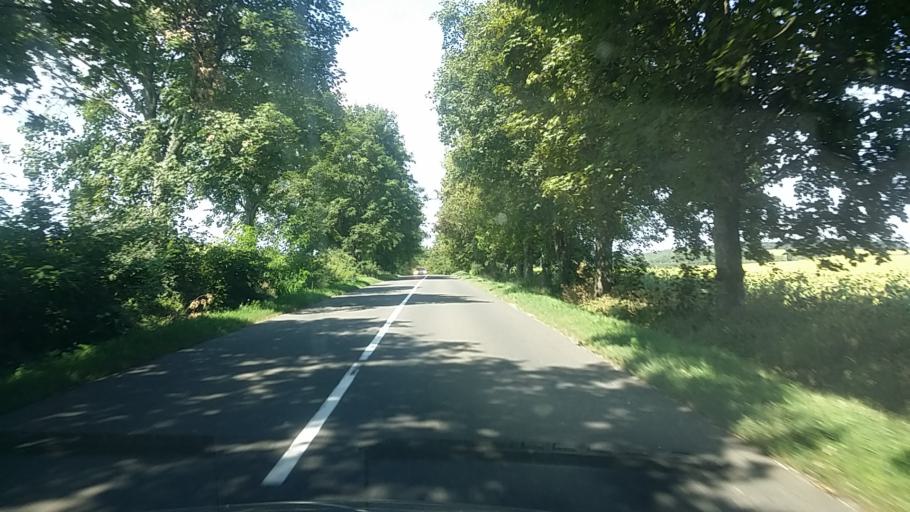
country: HU
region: Nograd
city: Retsag
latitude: 47.9349
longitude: 19.1591
